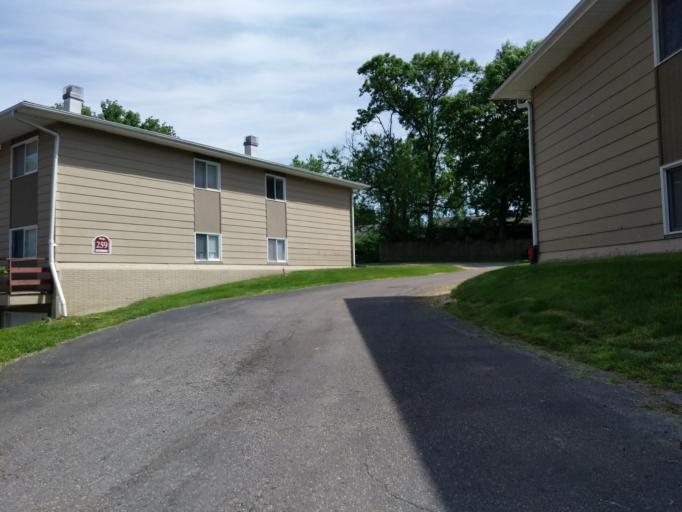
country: US
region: Iowa
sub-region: Linn County
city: Cedar Rapids
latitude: 42.0146
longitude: -91.6308
